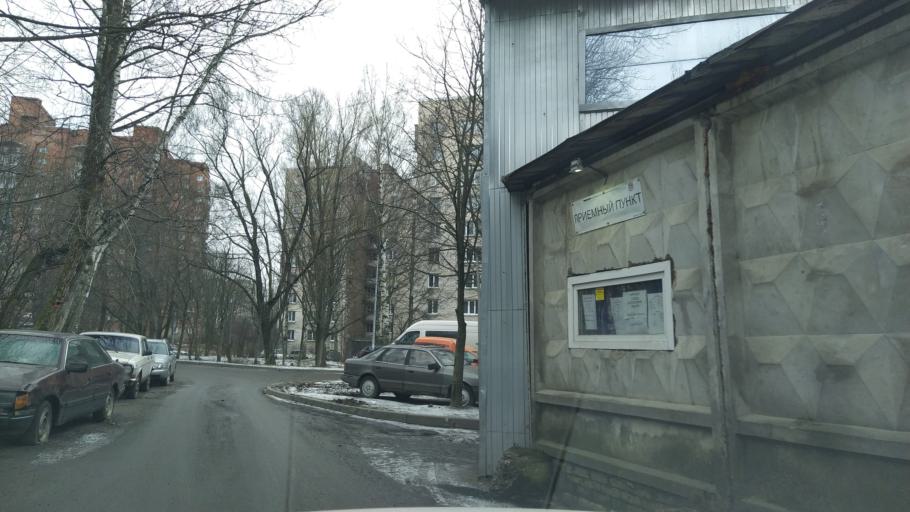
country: RU
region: Leningrad
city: Udel'naya
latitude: 60.0194
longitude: 30.3305
